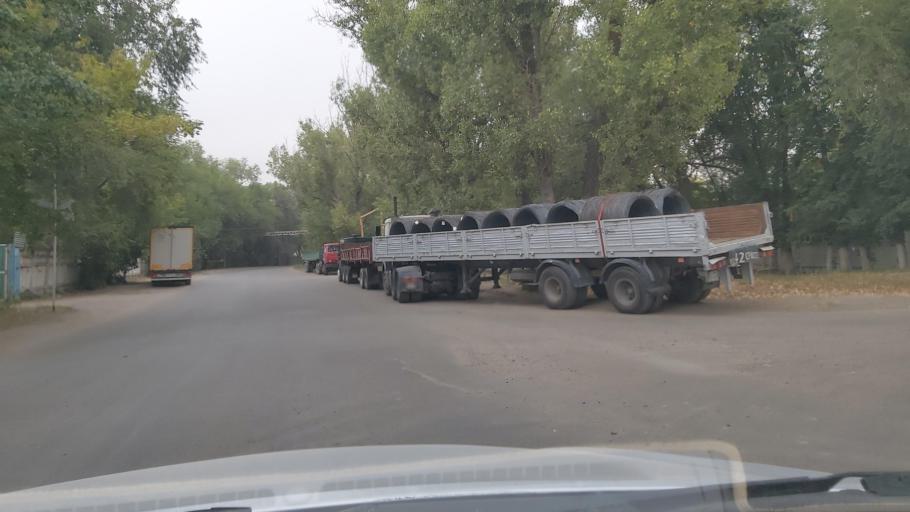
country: KZ
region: Almaty Oblysy
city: Pervomayskiy
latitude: 43.3505
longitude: 76.9745
